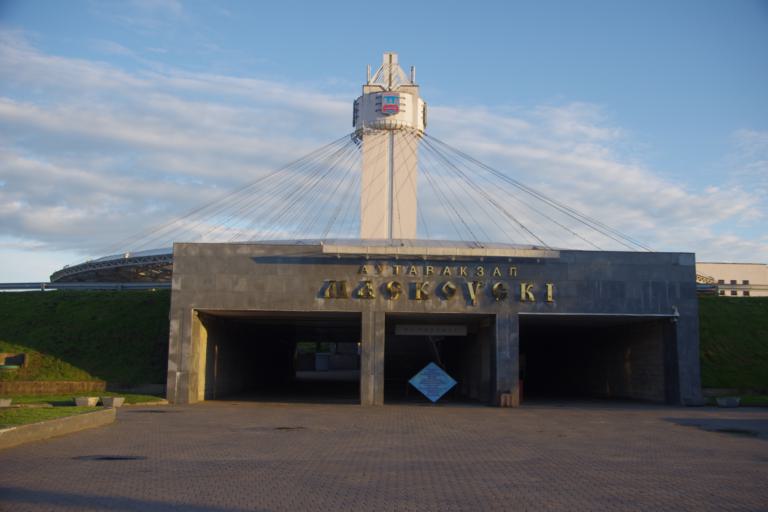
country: BY
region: Minsk
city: Minsk
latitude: 53.9295
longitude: 27.6370
